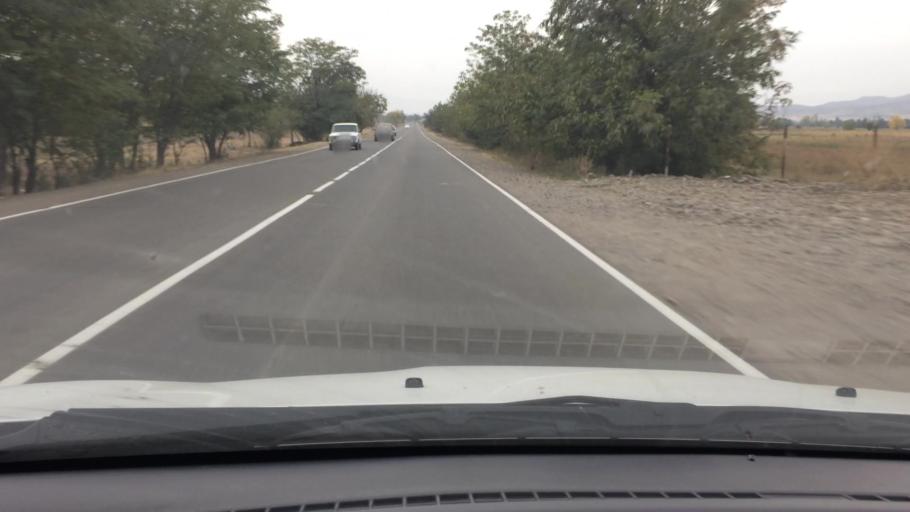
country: GE
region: Kvemo Kartli
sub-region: Marneuli
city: Marneuli
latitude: 41.4292
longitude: 44.8217
